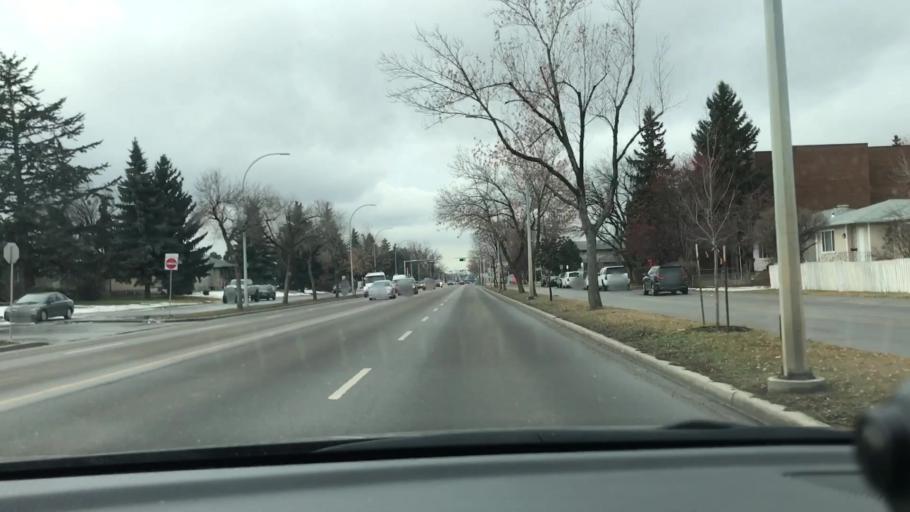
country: CA
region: Alberta
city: Edmonton
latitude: 53.5181
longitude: -113.4461
